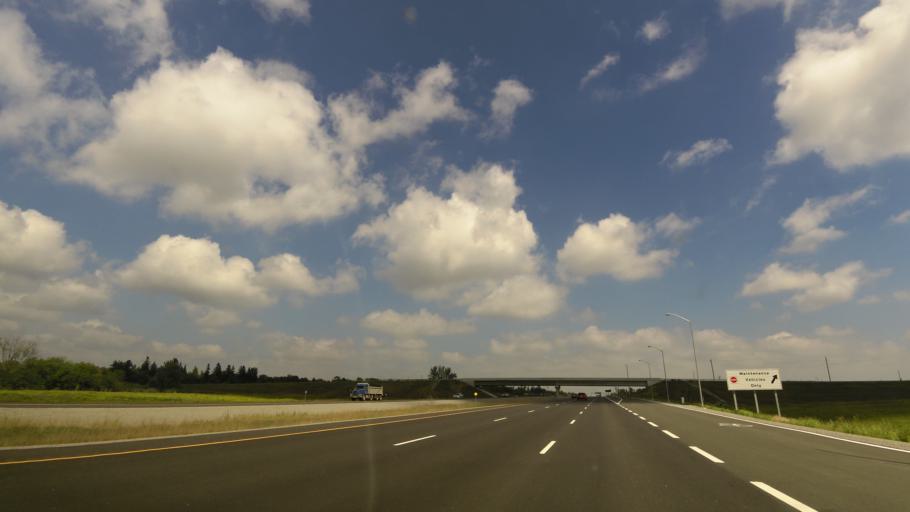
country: CA
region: Ontario
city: Pickering
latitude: 43.9419
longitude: -79.0537
